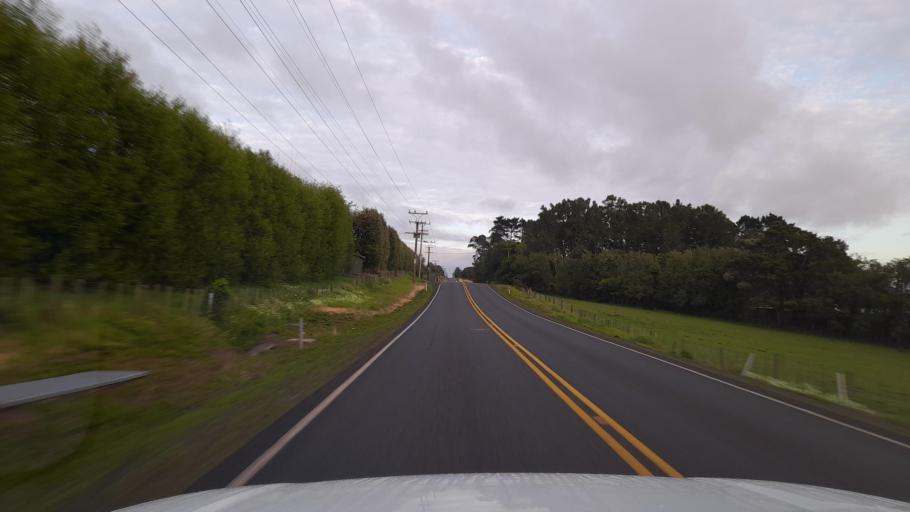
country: NZ
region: Northland
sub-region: Whangarei
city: Maungatapere
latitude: -35.7531
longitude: 174.1723
